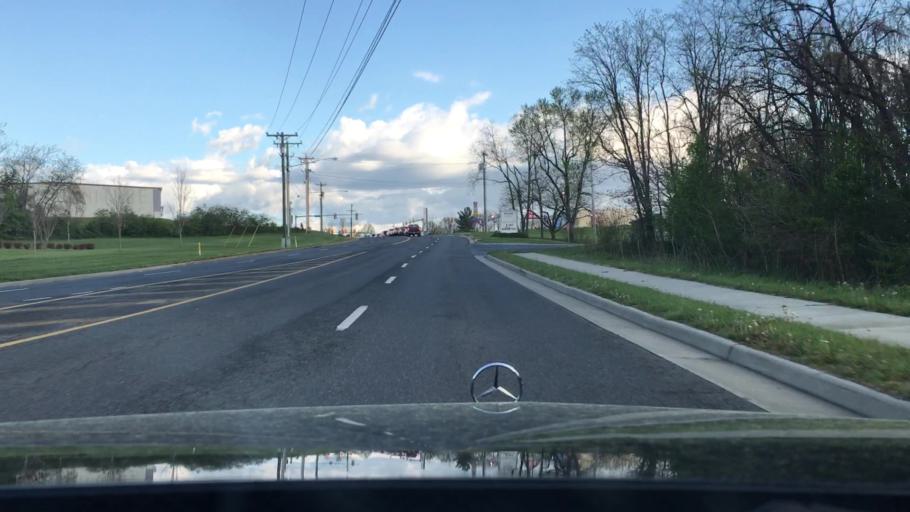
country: US
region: Virginia
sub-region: Campbell County
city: Timberlake
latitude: 37.3430
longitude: -79.2326
